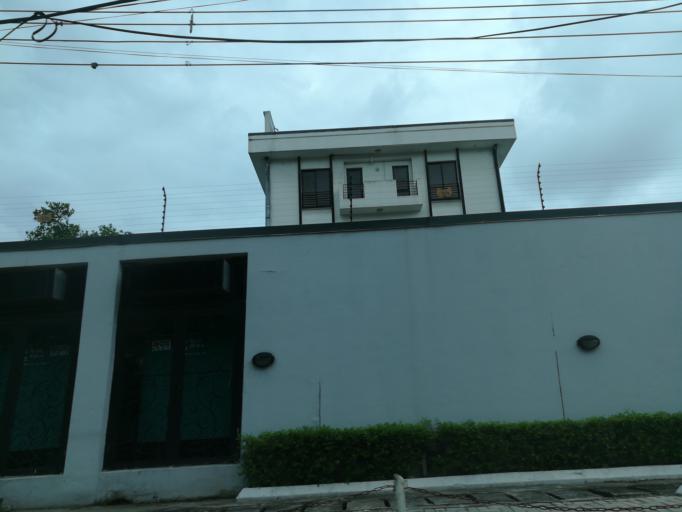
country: NG
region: Lagos
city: Ikoyi
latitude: 6.4336
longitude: 3.4152
